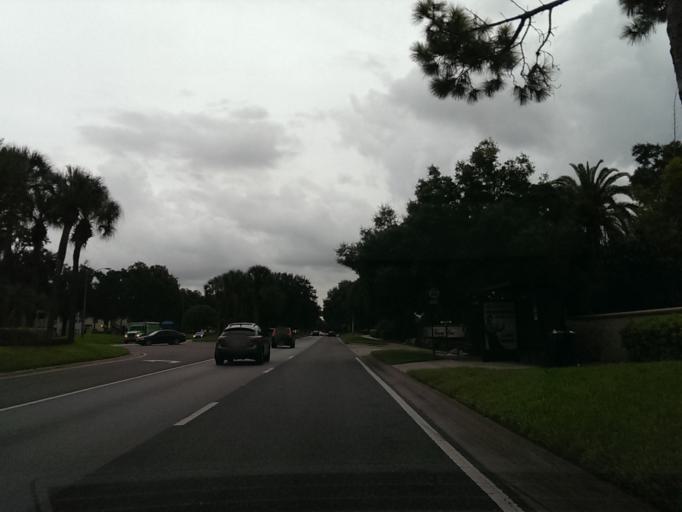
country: US
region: Florida
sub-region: Orange County
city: Orlovista
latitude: 28.5281
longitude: -81.4743
